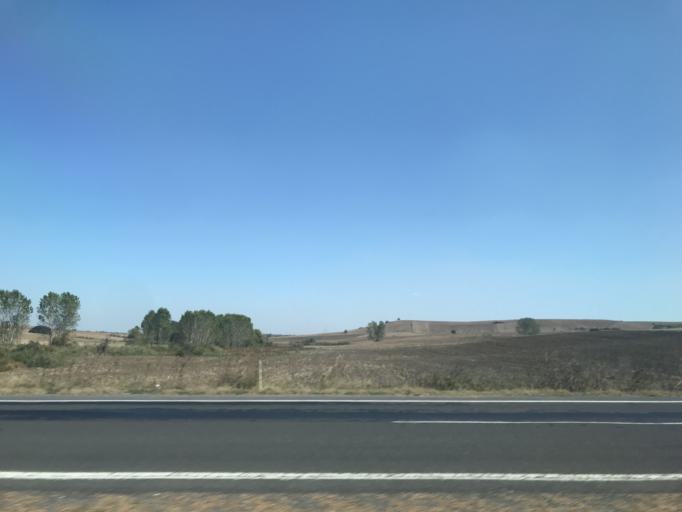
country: TR
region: Tekirdag
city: Muratli
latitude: 41.1008
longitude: 27.4945
